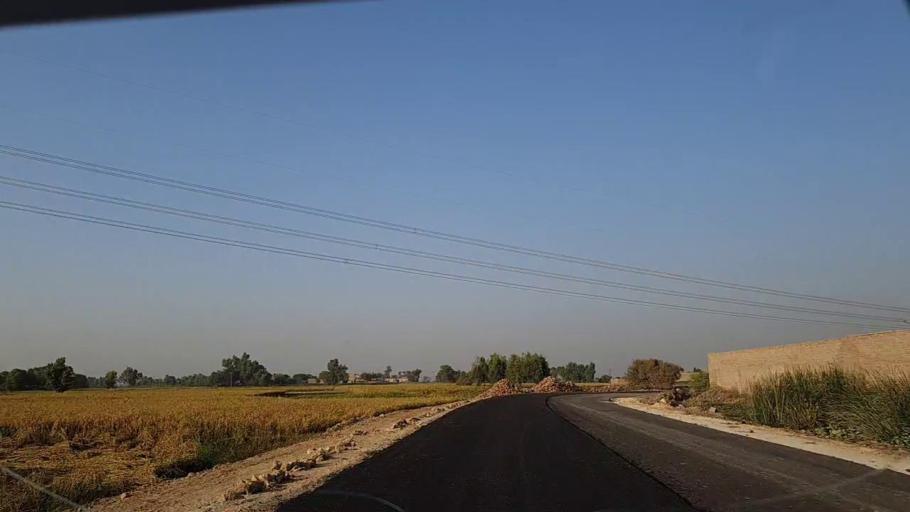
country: PK
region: Sindh
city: Rustam jo Goth
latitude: 27.9690
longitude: 68.8017
